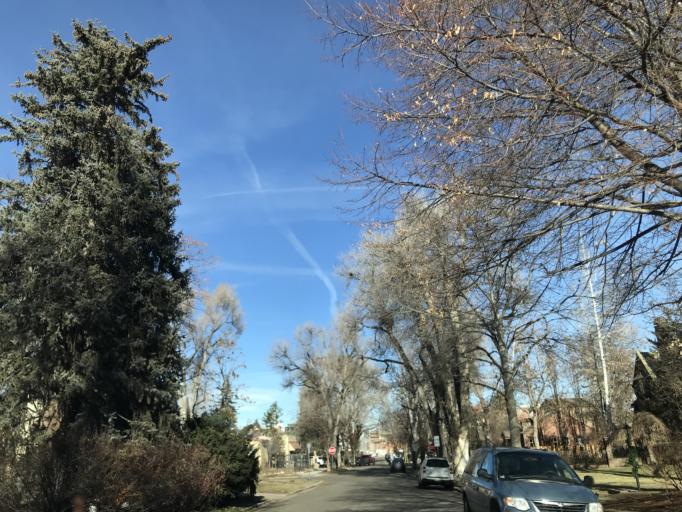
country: US
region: Colorado
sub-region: Arapahoe County
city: Glendale
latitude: 39.7268
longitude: -104.9371
